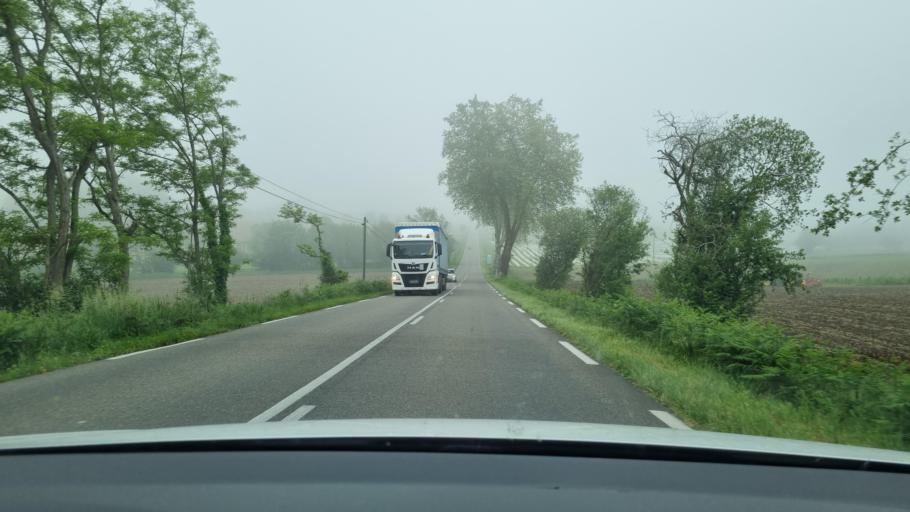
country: FR
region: Aquitaine
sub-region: Departement des Landes
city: Amou
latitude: 43.5672
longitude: -0.6623
